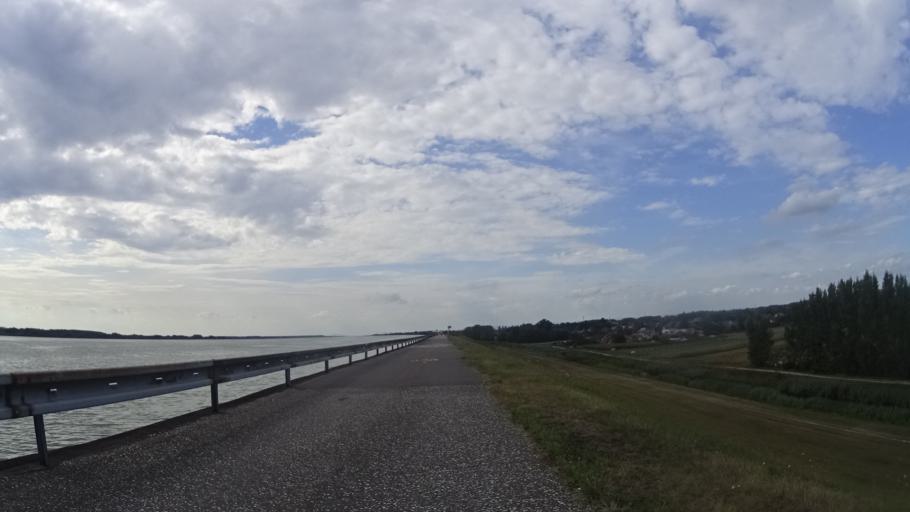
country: SK
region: Trnavsky
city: Gabcikovo
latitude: 47.8952
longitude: 17.5274
